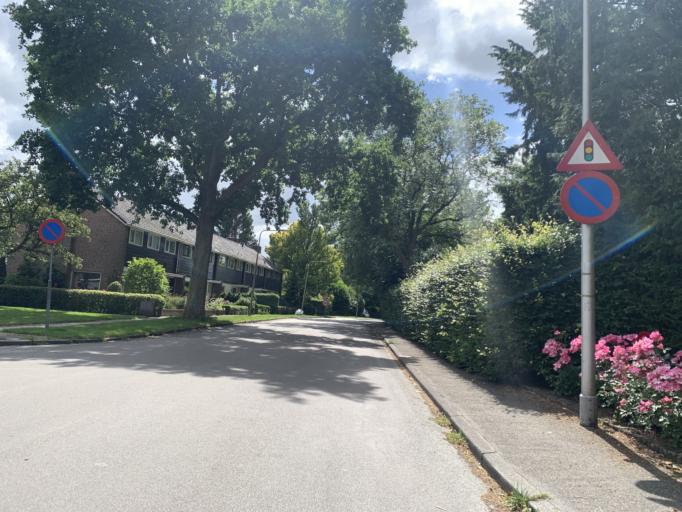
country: NL
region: Groningen
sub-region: Gemeente Haren
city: Haren
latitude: 53.1667
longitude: 6.6111
